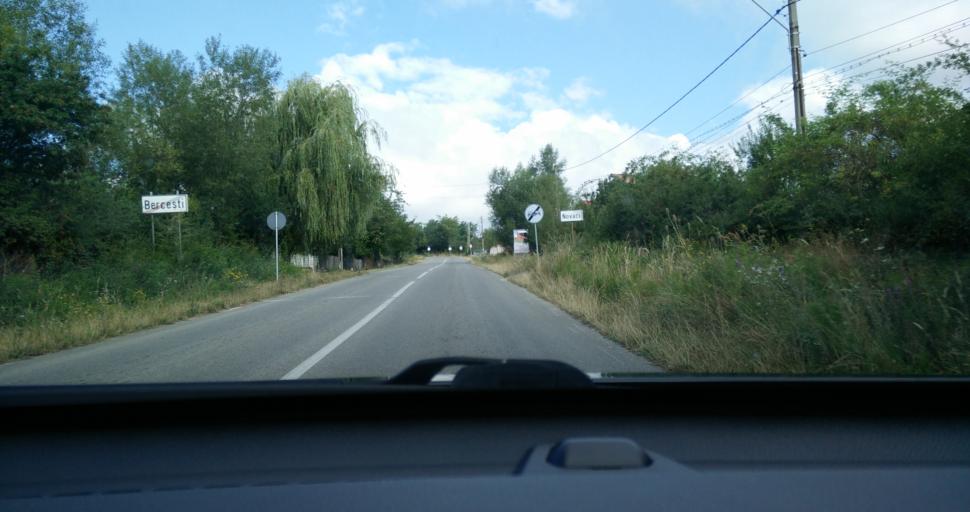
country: RO
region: Gorj
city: Novaci-Straini
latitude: 45.1786
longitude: 23.6972
